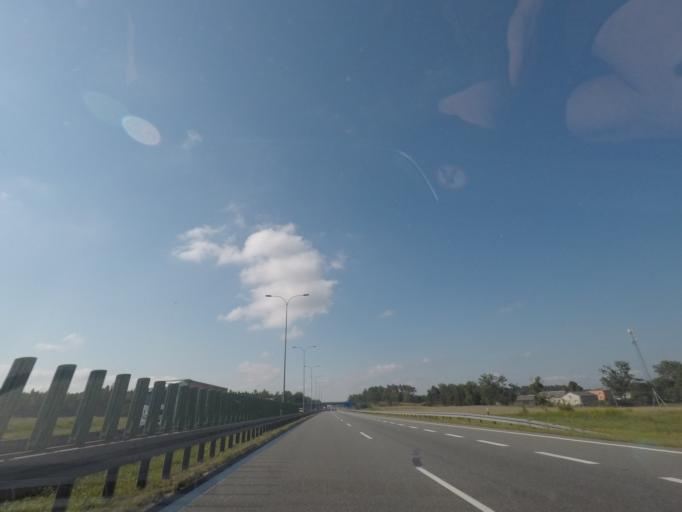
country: PL
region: Pomeranian Voivodeship
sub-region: Powiat tczewski
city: Pelplin
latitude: 54.0255
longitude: 18.6688
